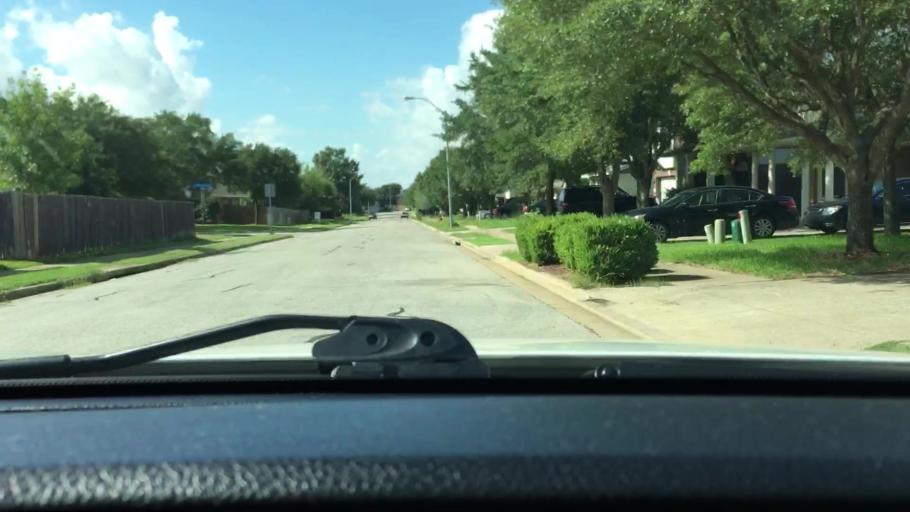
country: US
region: Texas
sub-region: Travis County
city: Windemere
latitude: 30.4770
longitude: -97.6476
